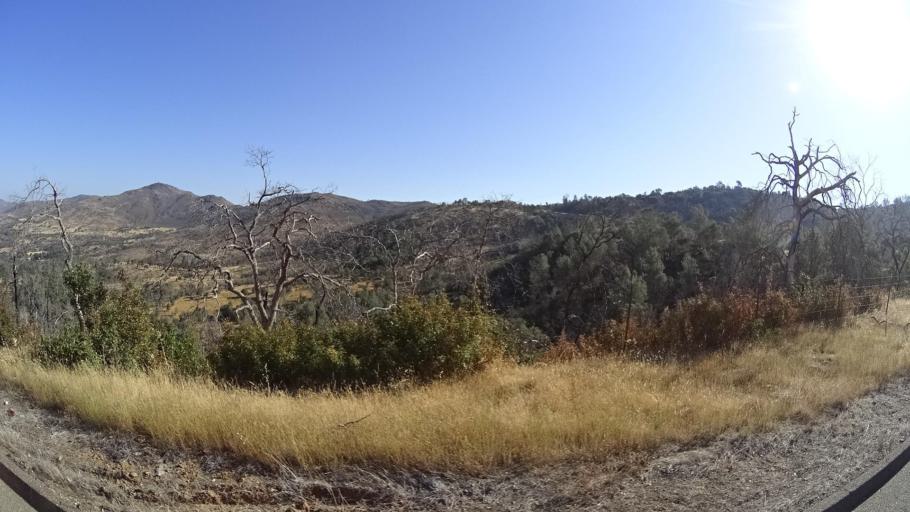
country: US
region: California
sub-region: Mariposa County
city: Mariposa
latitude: 37.5642
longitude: -120.1636
